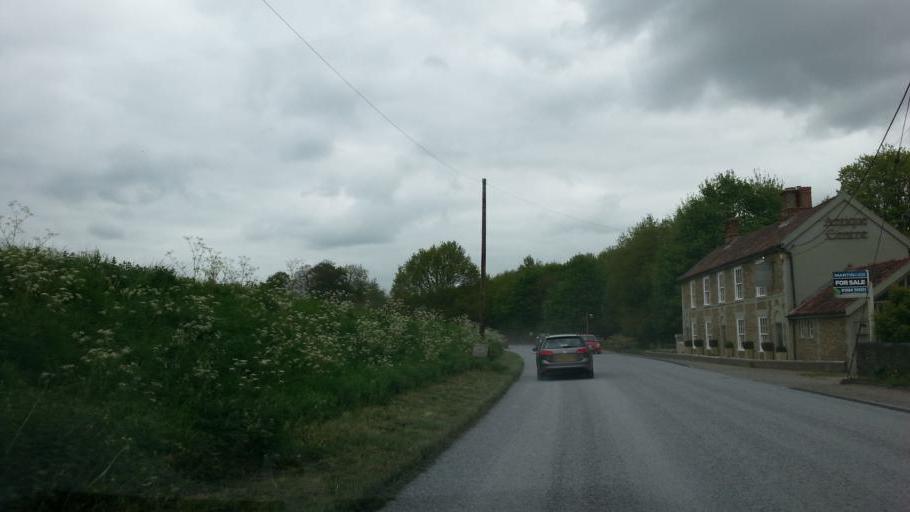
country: GB
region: England
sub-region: Suffolk
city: Bury St Edmunds
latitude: 52.2052
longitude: 0.7560
